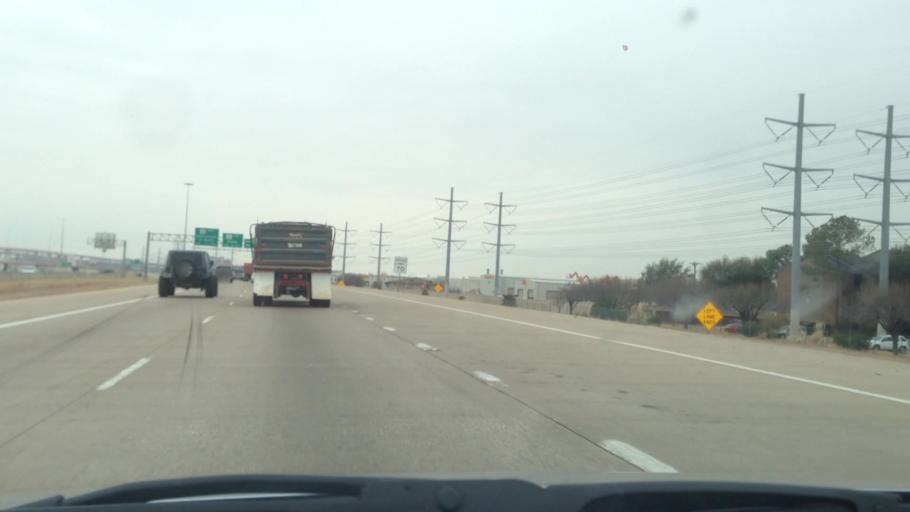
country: US
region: Texas
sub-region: Tarrant County
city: Euless
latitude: 32.8528
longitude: -97.0160
